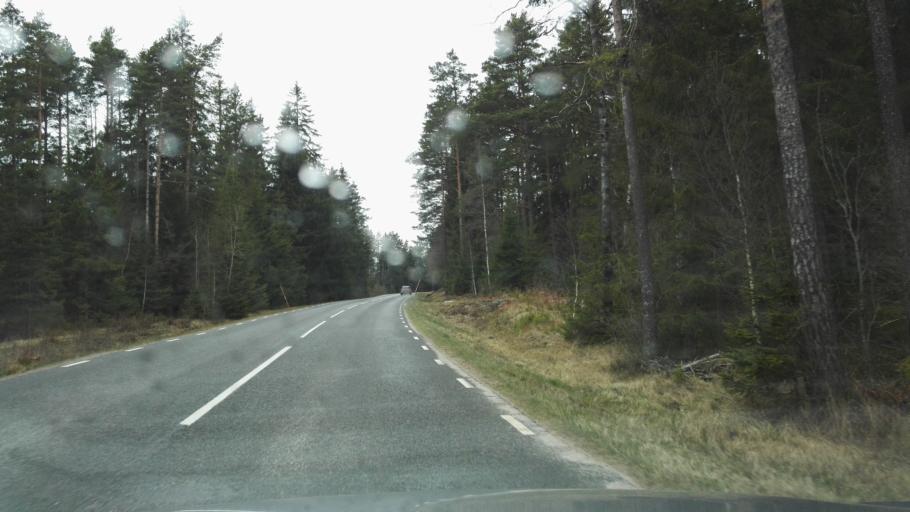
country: SE
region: Joenkoeping
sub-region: Vetlanda Kommun
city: Landsbro
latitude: 57.2790
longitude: 14.8925
